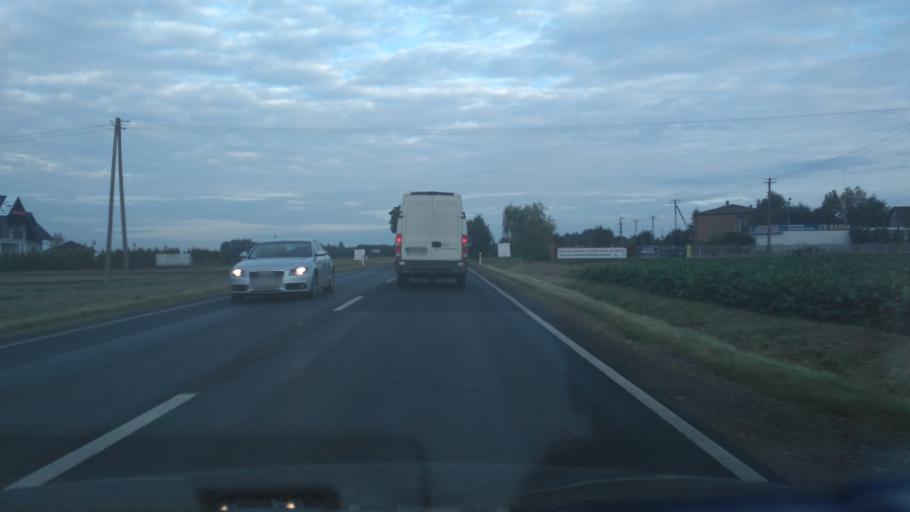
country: PL
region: Lublin Voivodeship
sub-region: Powiat leczynski
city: Spiczyn
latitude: 51.2995
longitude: 22.7625
